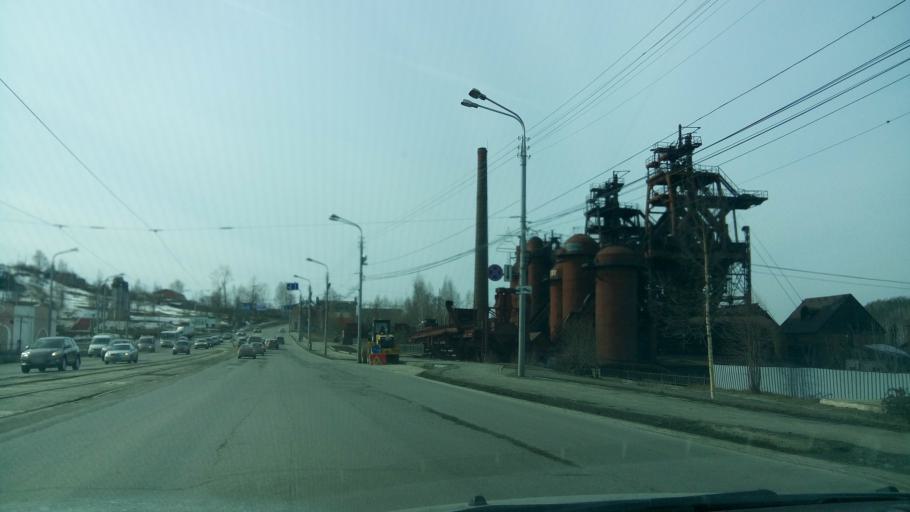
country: RU
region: Sverdlovsk
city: Nizhniy Tagil
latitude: 57.9042
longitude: 59.9495
